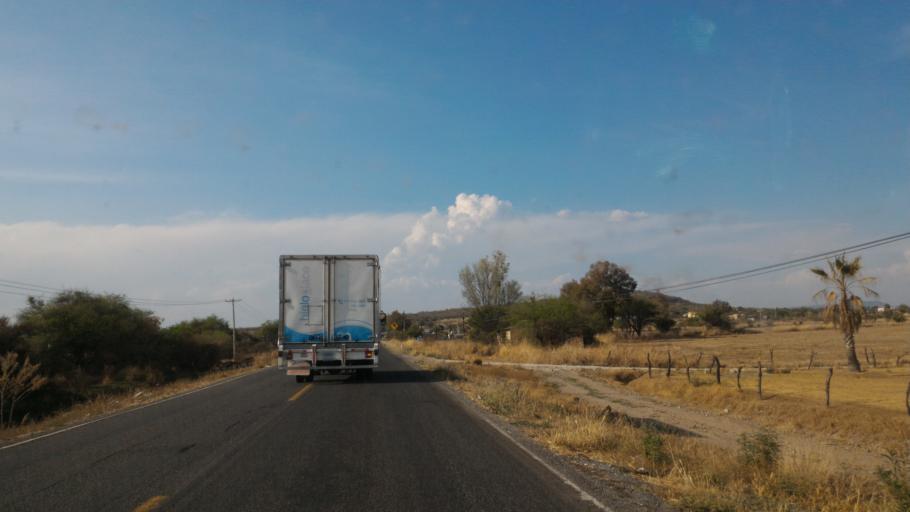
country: MX
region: Guanajuato
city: Ciudad Manuel Doblado
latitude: 20.7935
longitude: -101.9840
